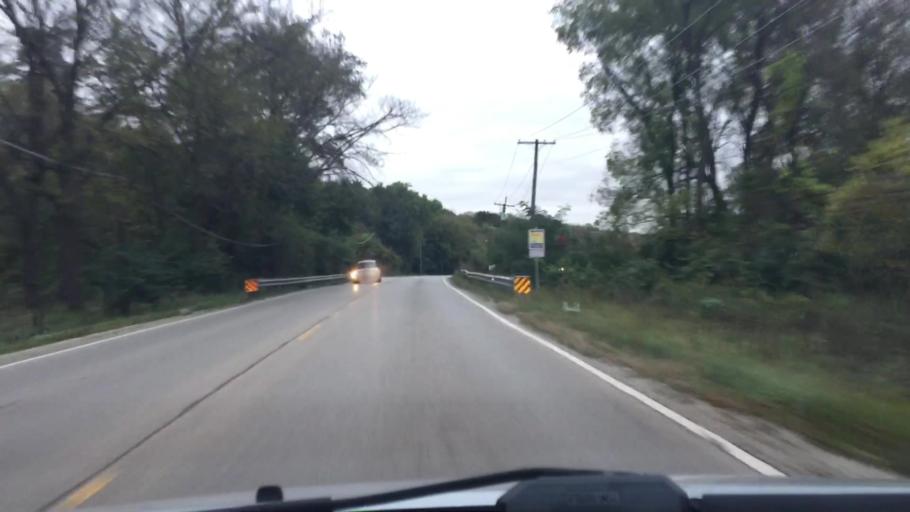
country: US
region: Illinois
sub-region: Kane County
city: Sleepy Hollow
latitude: 42.1193
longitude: -88.2988
